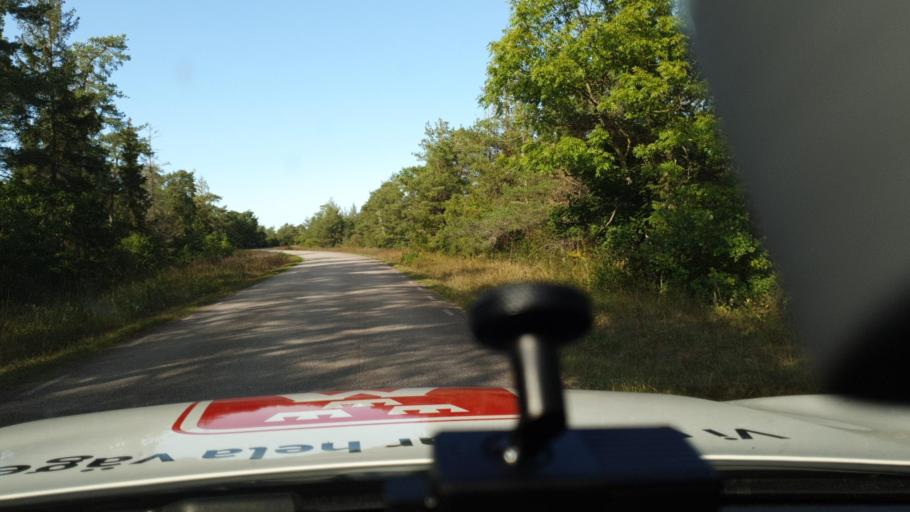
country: SE
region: Gotland
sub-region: Gotland
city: Slite
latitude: 57.6869
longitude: 18.6371
